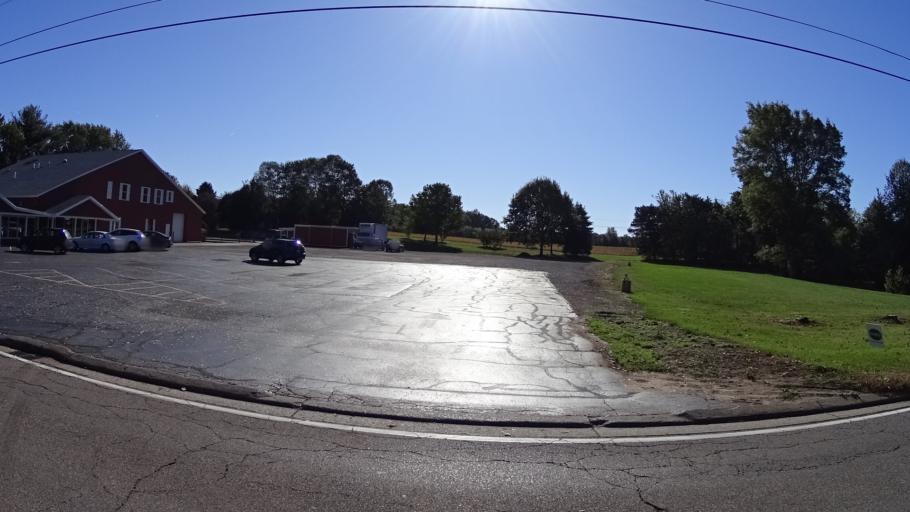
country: US
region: Ohio
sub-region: Lorain County
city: Lorain
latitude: 41.4155
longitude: -82.1889
